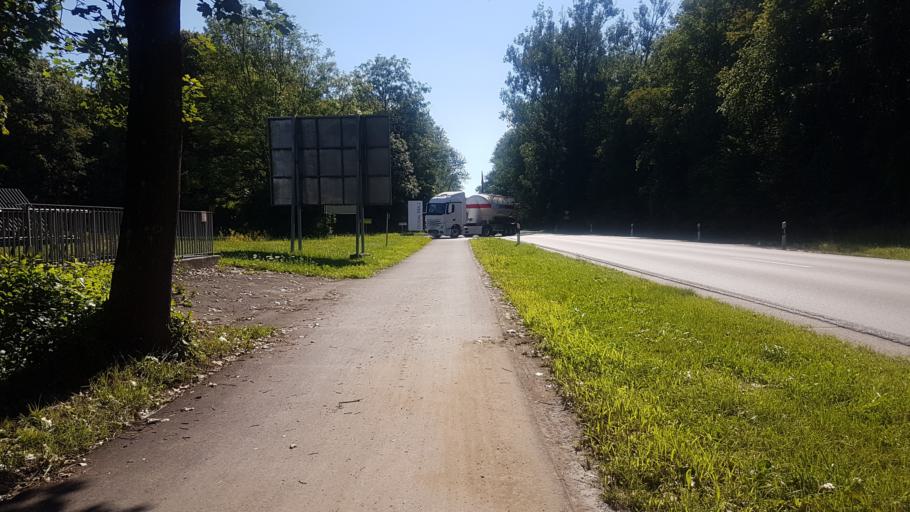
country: DE
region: Bavaria
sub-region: Upper Bavaria
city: Bergheim
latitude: 48.7377
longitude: 11.2482
